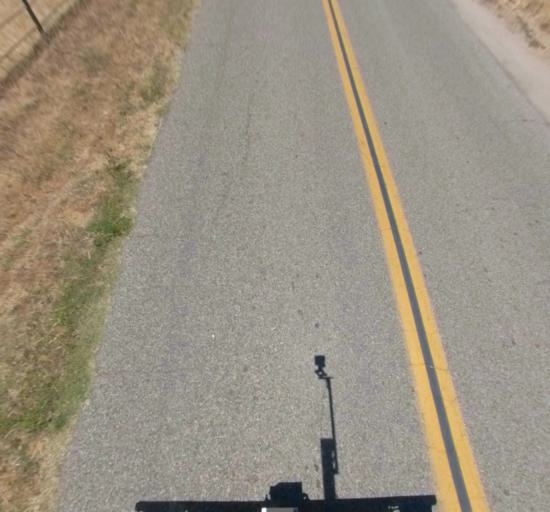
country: US
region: California
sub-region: Madera County
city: Chowchilla
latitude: 37.0913
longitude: -120.2861
